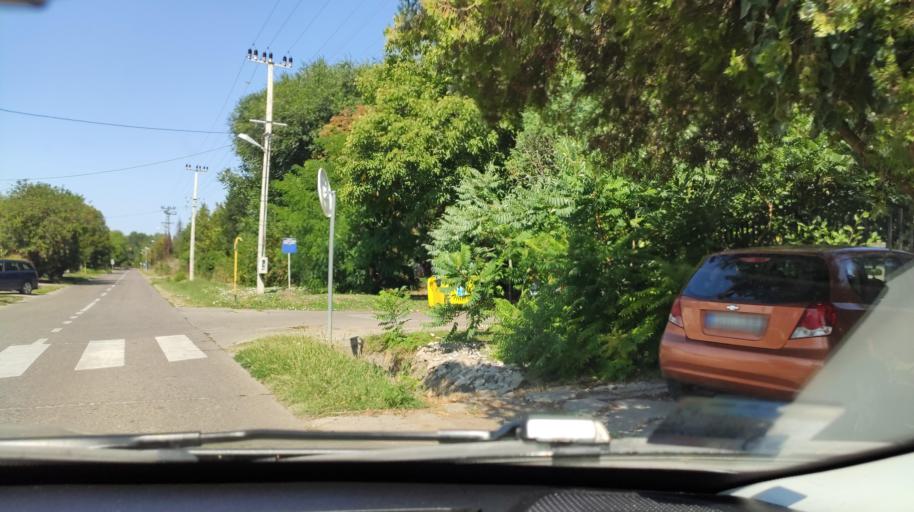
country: RS
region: Autonomna Pokrajina Vojvodina
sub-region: Severnobacki Okrug
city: Backa Topola
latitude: 45.8215
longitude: 19.6353
